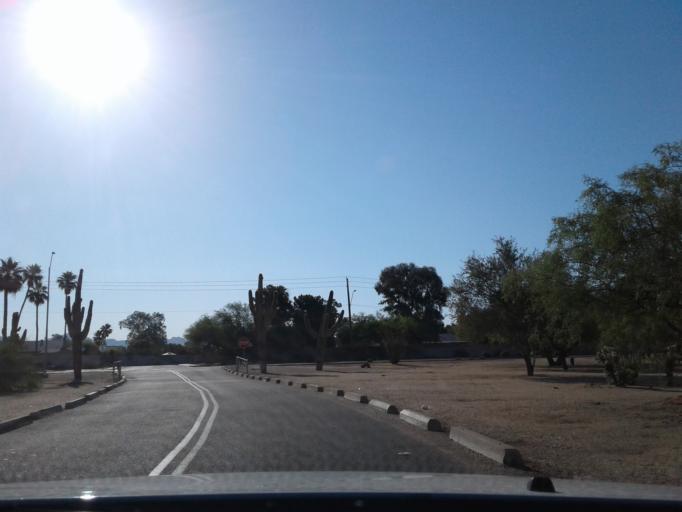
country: US
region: Arizona
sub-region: Maricopa County
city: Paradise Valley
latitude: 33.6462
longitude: -111.9970
